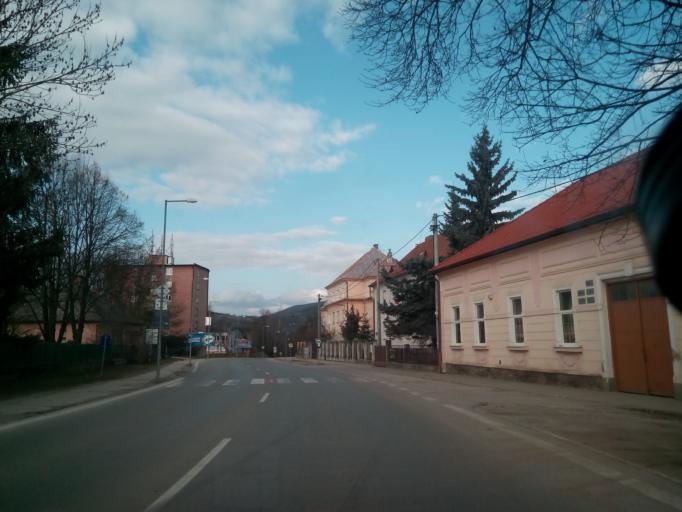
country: SK
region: Kosicky
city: Roznava
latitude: 48.6591
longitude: 20.5292
